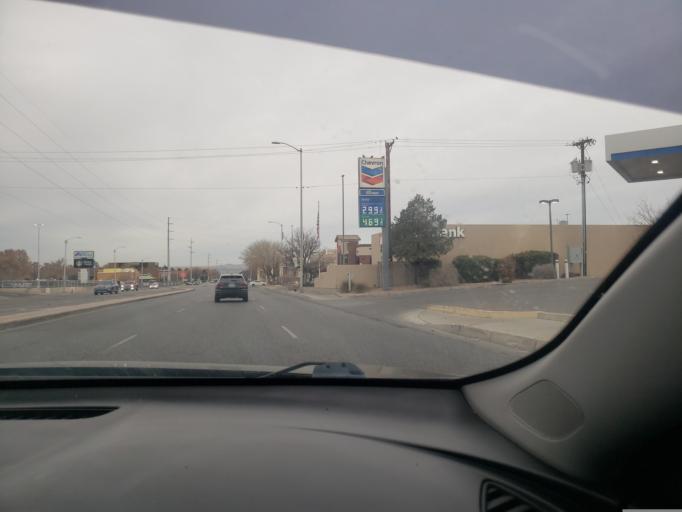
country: US
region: New Mexico
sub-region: Bernalillo County
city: North Valley
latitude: 35.1311
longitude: -106.5867
